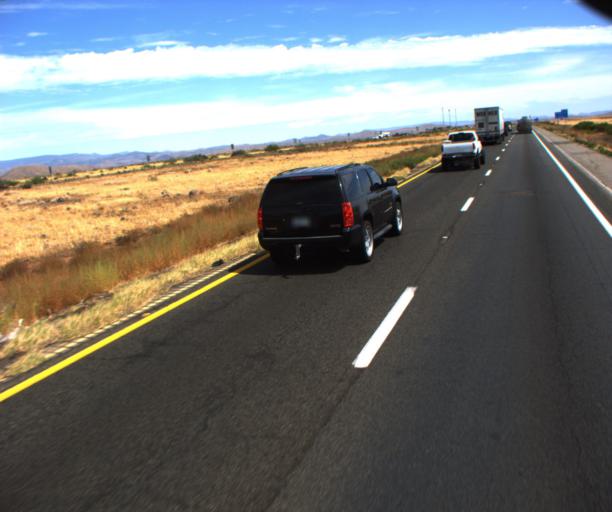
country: US
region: Arizona
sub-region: Yavapai County
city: Black Canyon City
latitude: 34.1746
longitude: -112.1354
